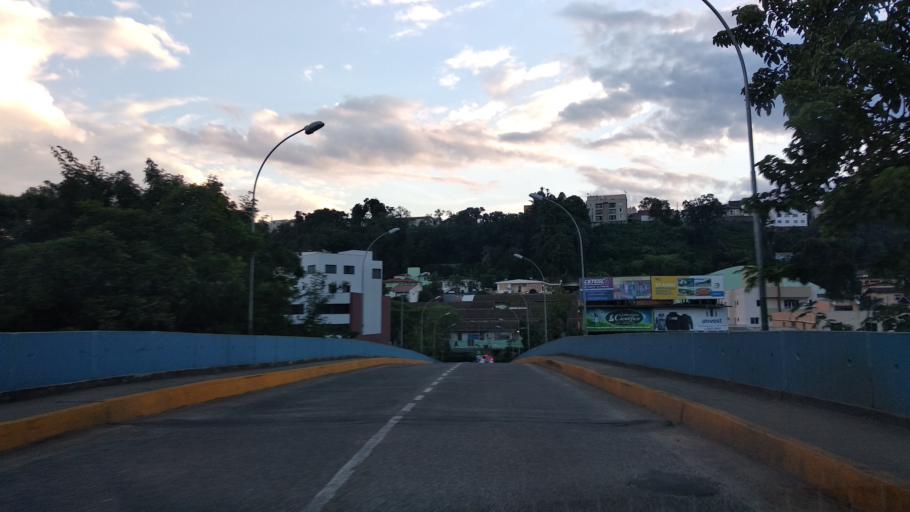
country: BR
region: Santa Catarina
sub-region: Videira
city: Videira
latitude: -27.0012
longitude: -51.1570
